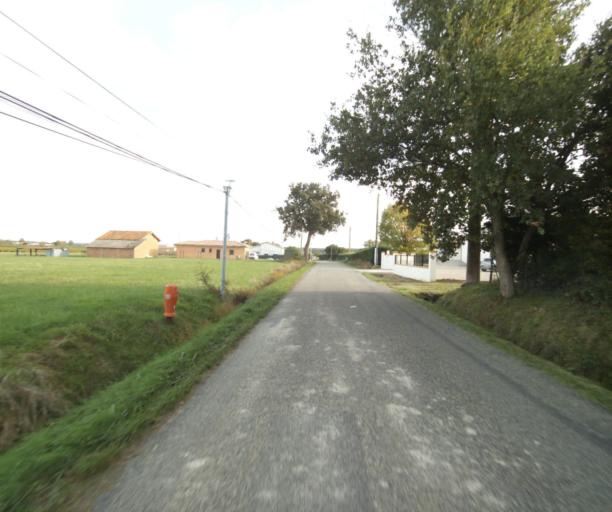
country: FR
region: Midi-Pyrenees
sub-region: Departement du Tarn-et-Garonne
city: Campsas
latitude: 43.8840
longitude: 1.3357
